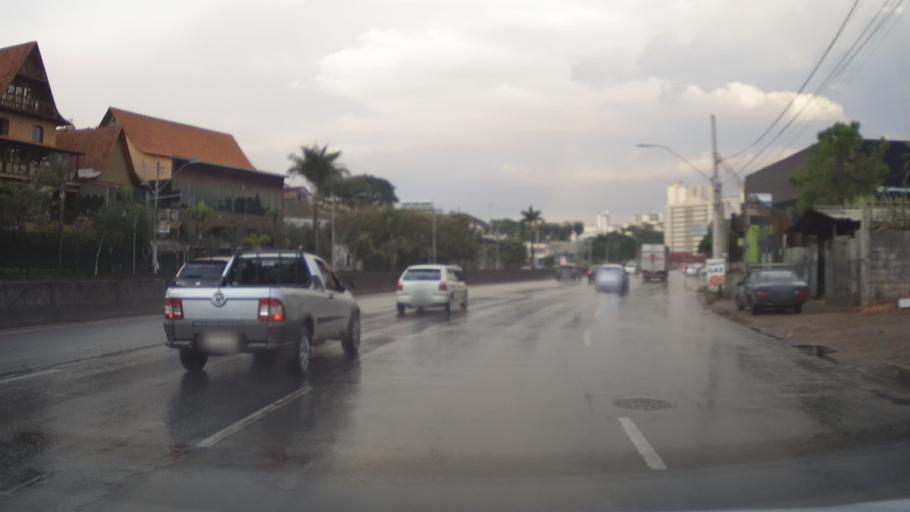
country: BR
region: Minas Gerais
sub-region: Belo Horizonte
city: Belo Horizonte
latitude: -19.9422
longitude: -43.9874
